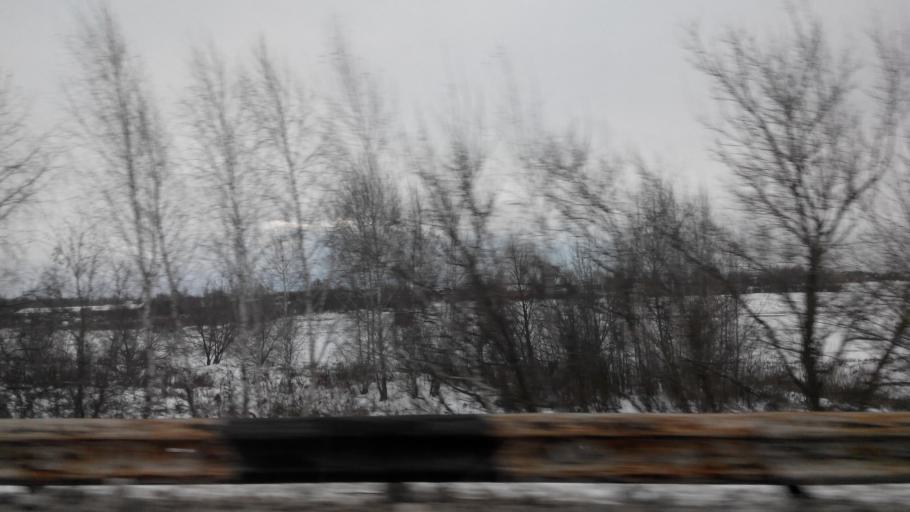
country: RU
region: Tula
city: Mayskiy
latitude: 53.9803
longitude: 38.2254
